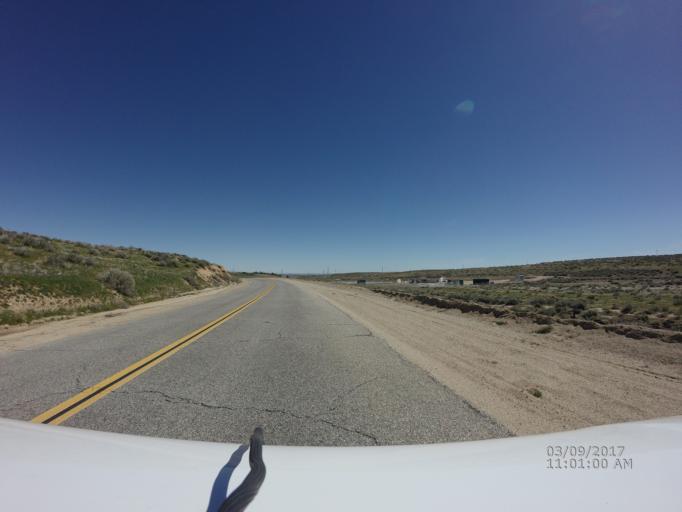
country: US
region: California
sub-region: Los Angeles County
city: Green Valley
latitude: 34.7056
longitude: -118.3659
